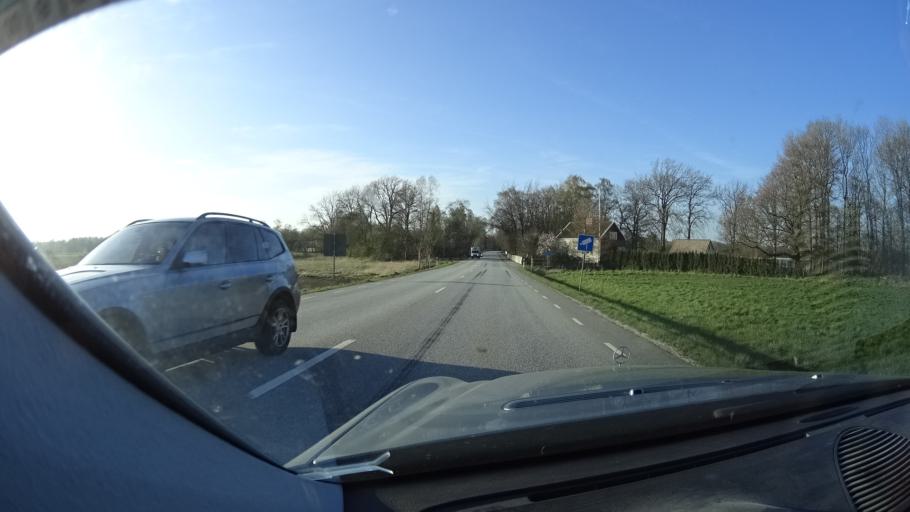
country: SE
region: Skane
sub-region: Hoors Kommun
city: Satofta
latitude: 55.8682
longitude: 13.4957
